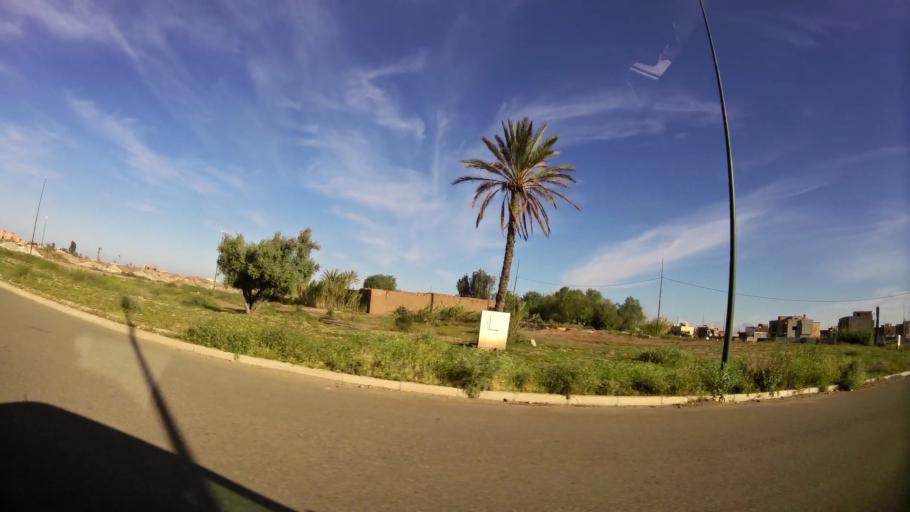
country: MA
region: Marrakech-Tensift-Al Haouz
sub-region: Marrakech
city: Marrakesh
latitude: 31.6747
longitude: -8.0715
